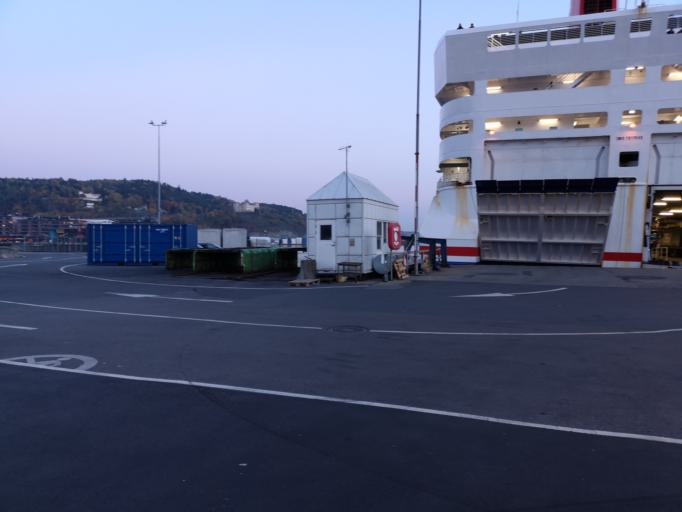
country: NO
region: Oslo
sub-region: Oslo
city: Oslo
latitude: 59.9041
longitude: 10.7435
